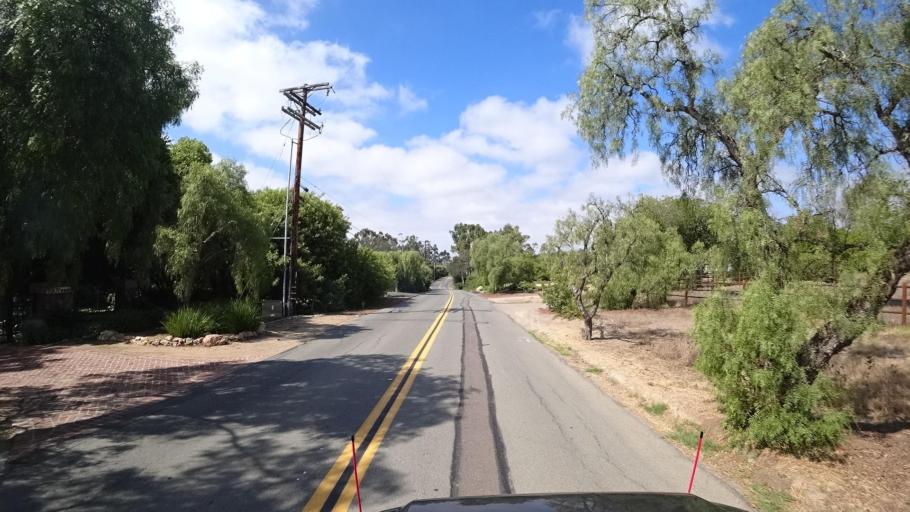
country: US
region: California
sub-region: San Diego County
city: Rancho Santa Fe
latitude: 33.0254
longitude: -117.2071
